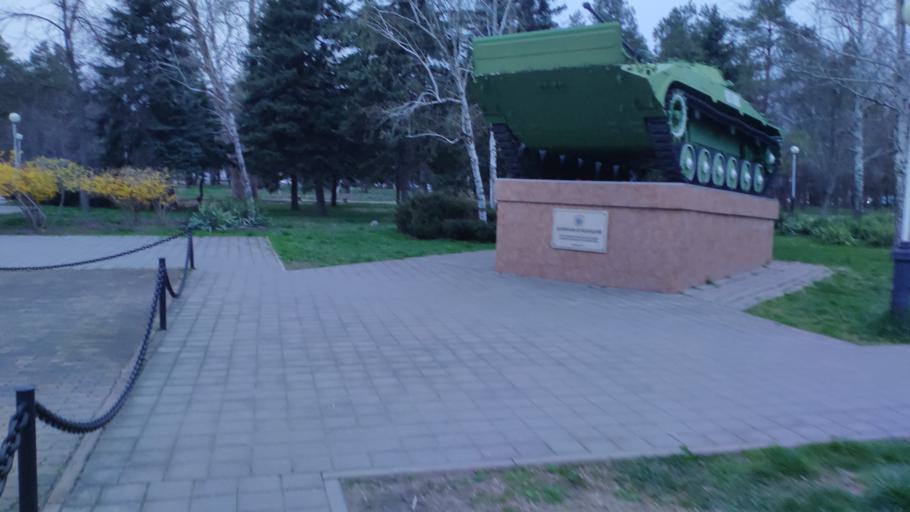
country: RU
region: Krasnodarskiy
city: Krasnodar
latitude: 45.0604
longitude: 38.9911
